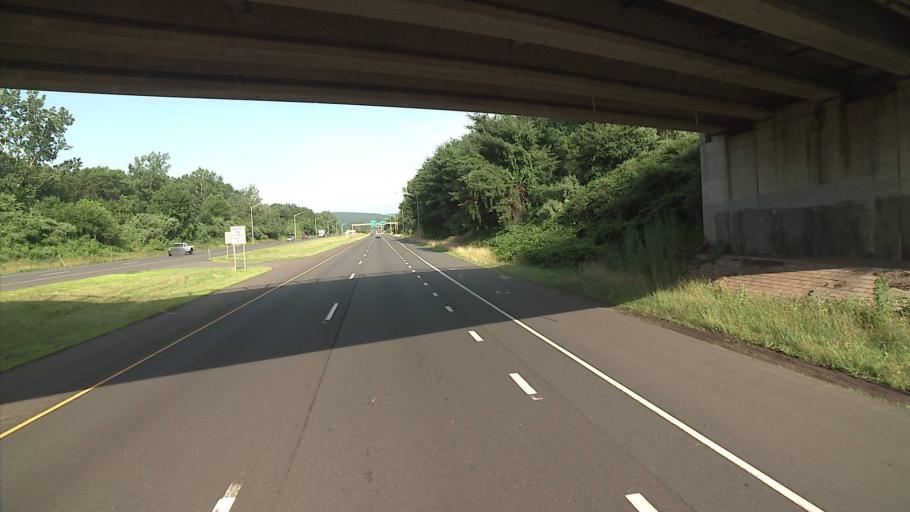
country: US
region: Connecticut
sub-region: New Haven County
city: Cheshire Village
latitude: 41.5583
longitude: -72.9030
